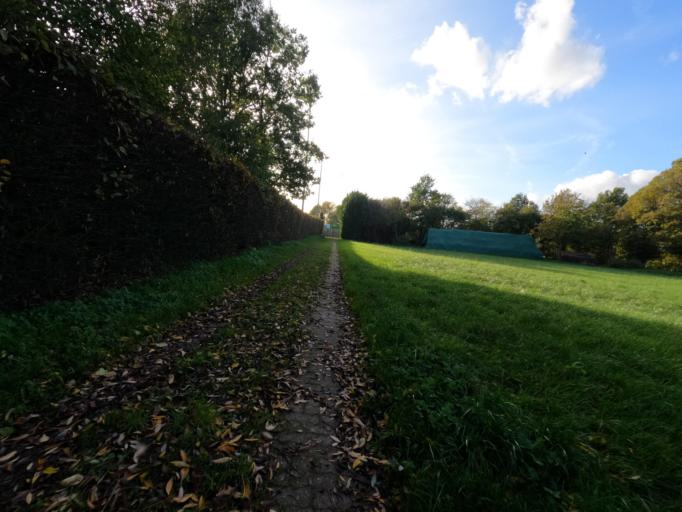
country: DE
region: North Rhine-Westphalia
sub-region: Regierungsbezirk Koln
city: Titz
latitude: 51.0456
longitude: 6.3973
